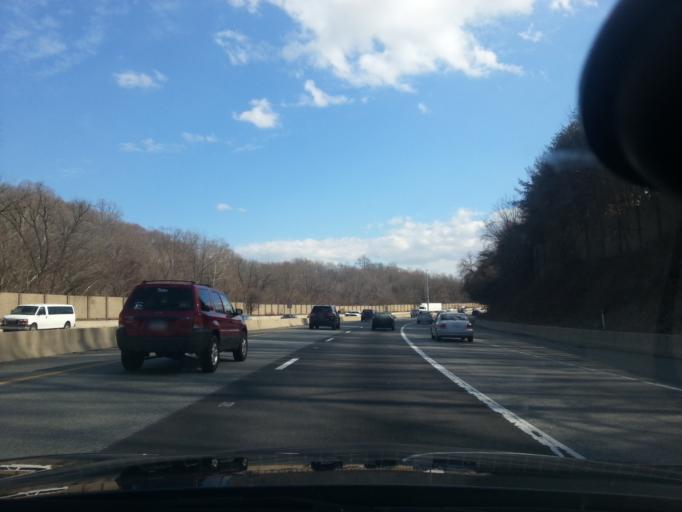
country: US
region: Pennsylvania
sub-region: Delaware County
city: Broomall
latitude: 39.9859
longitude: -75.3402
